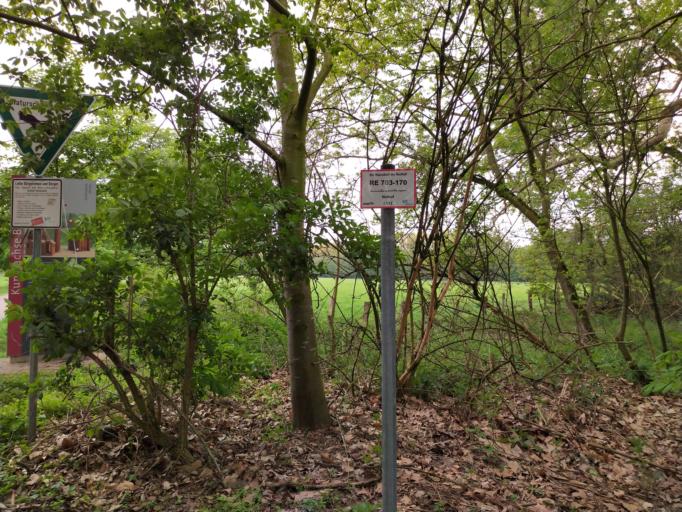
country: DE
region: North Rhine-Westphalia
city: Herten
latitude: 51.5893
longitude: 7.1284
